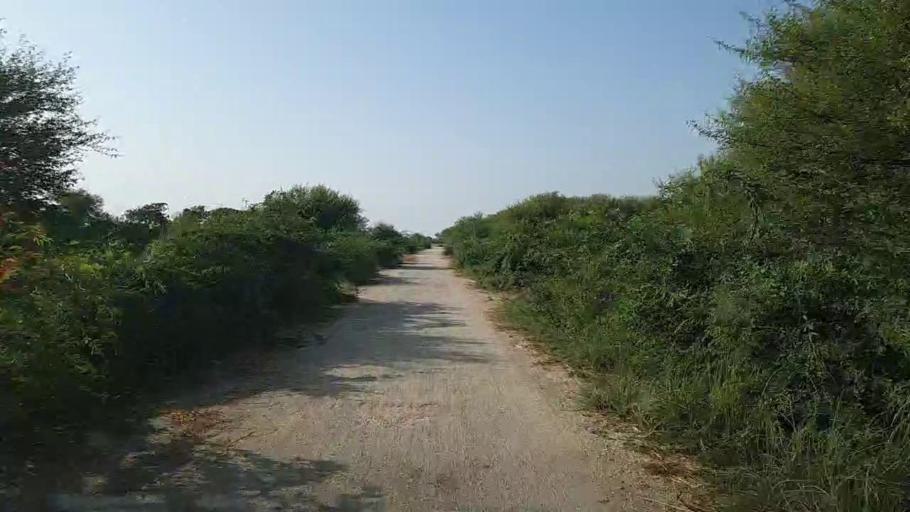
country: PK
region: Sindh
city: Kario
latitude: 24.8213
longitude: 68.4943
